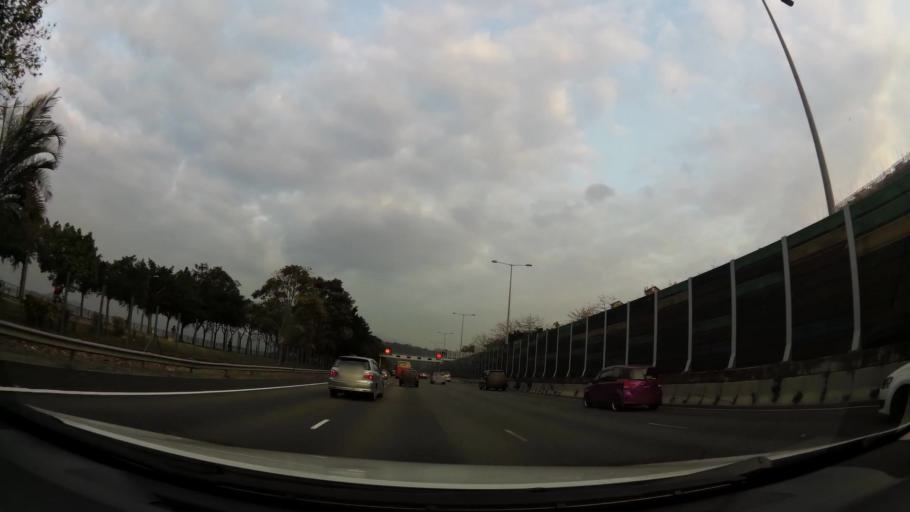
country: HK
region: Tai Po
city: Tai Po
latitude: 22.4425
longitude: 114.1816
